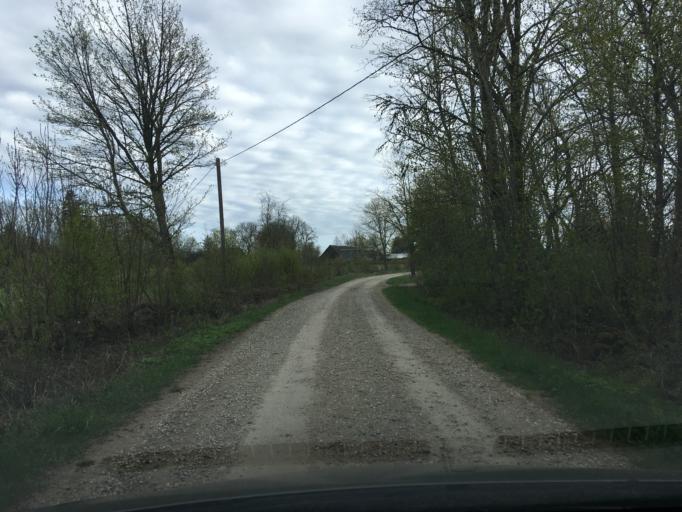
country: EE
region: Laeaene
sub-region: Lihula vald
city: Lihula
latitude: 58.5762
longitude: 23.7234
